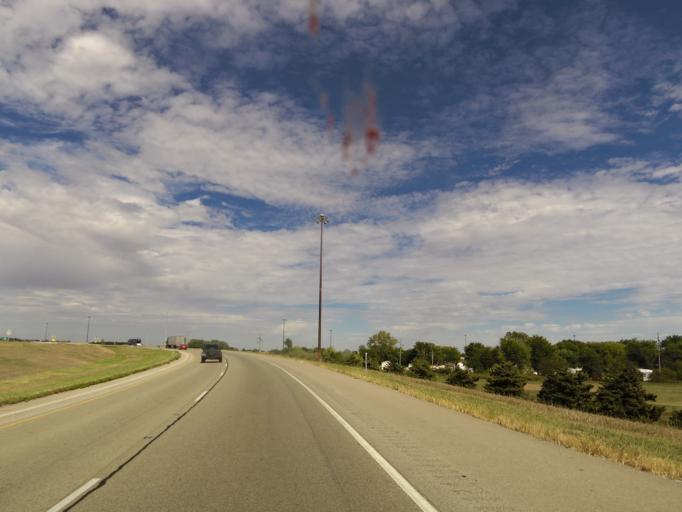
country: US
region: Illinois
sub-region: McLean County
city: Normal
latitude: 40.5366
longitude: -89.0043
